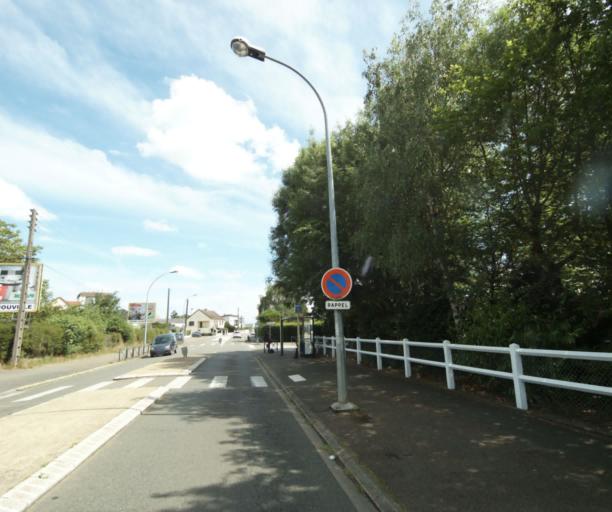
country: FR
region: Centre
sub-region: Departement d'Eure-et-Loir
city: Luce
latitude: 48.4349
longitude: 1.4559
